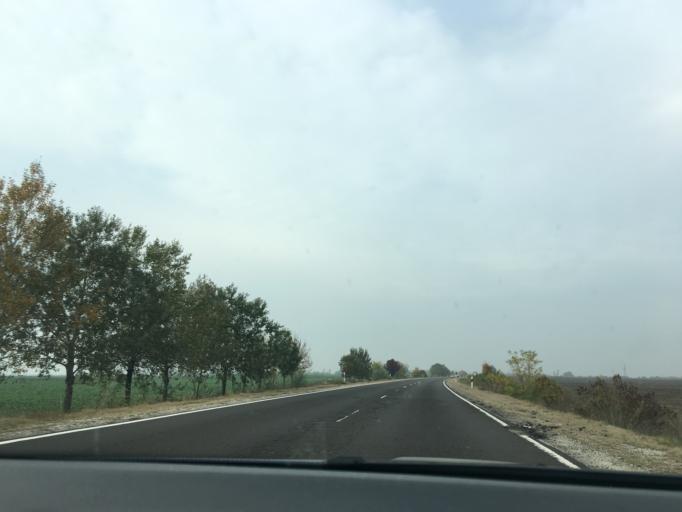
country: HU
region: Pest
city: Abony
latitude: 47.1983
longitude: 20.0795
